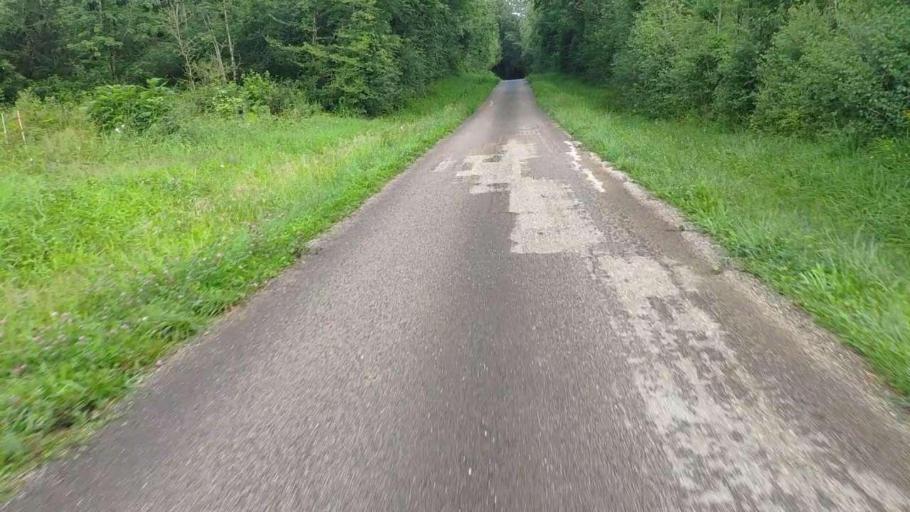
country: FR
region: Franche-Comte
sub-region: Departement du Jura
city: Poligny
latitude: 46.7969
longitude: 5.5996
